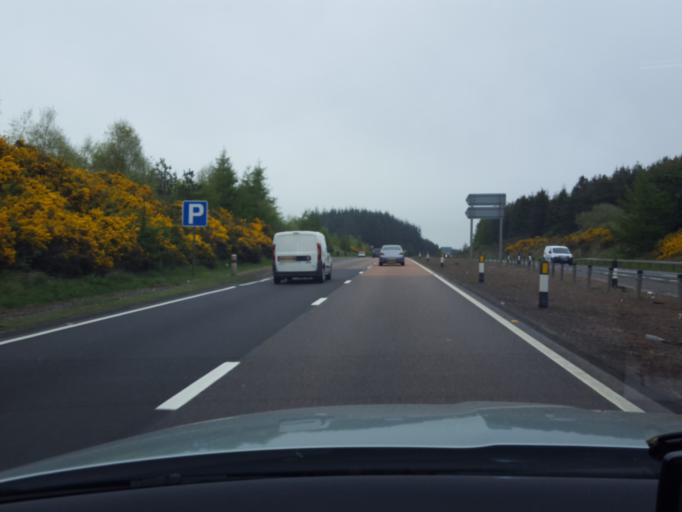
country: GB
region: Scotland
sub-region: Dundee City
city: Dundee
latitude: 56.5487
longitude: -2.9392
